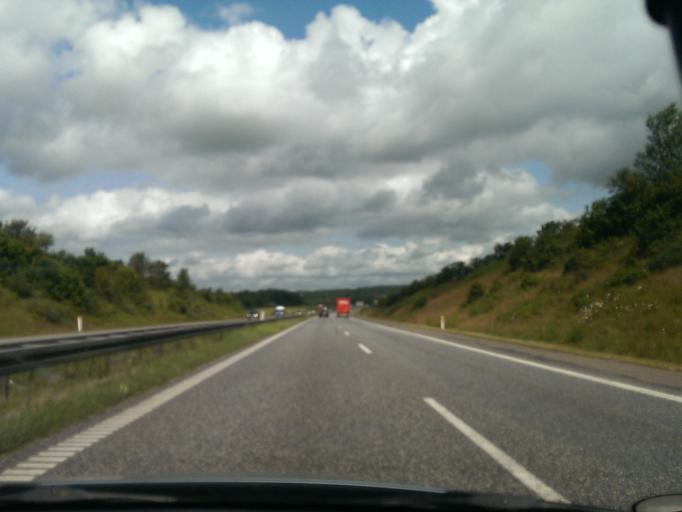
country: DK
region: North Denmark
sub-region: Mariagerfjord Kommune
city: Hobro
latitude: 56.6066
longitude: 9.7444
